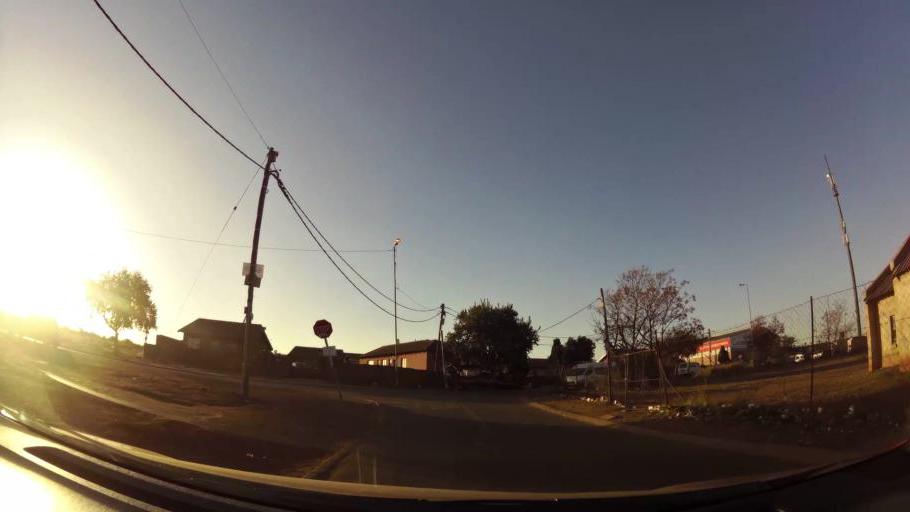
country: ZA
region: Gauteng
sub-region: City of Tshwane Metropolitan Municipality
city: Mabopane
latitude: -25.5824
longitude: 28.1025
